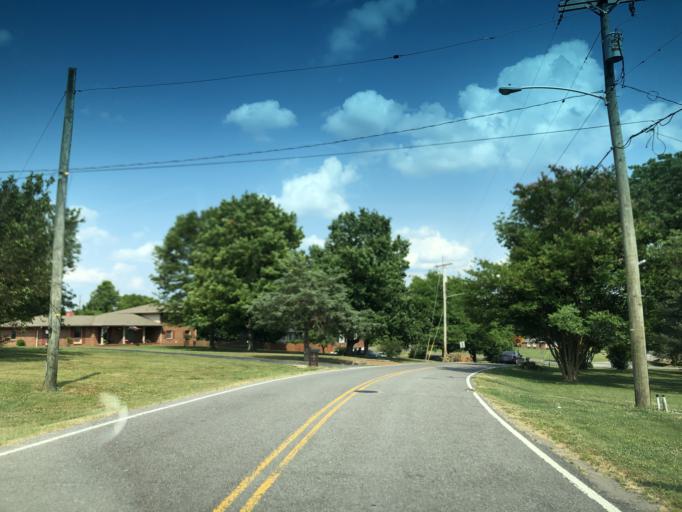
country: US
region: Tennessee
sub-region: Davidson County
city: Goodlettsville
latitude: 36.2458
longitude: -86.7323
